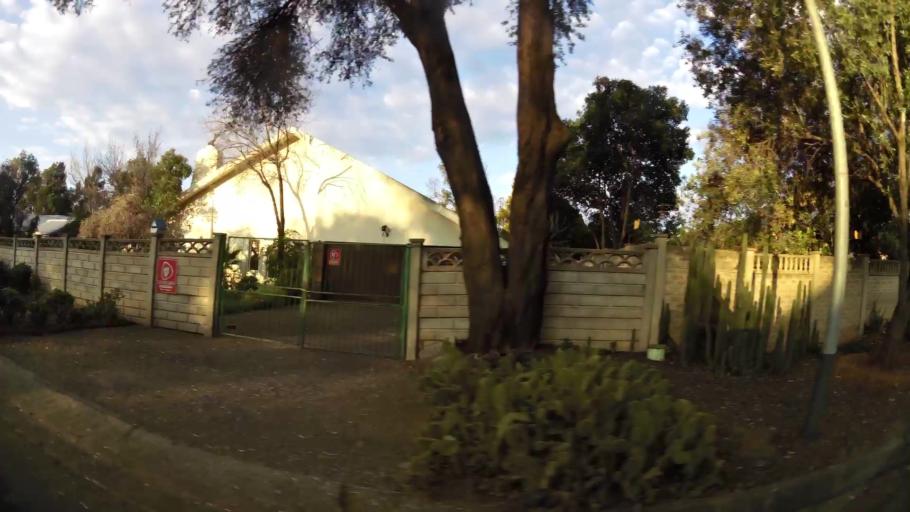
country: ZA
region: Orange Free State
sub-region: Mangaung Metropolitan Municipality
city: Bloemfontein
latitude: -29.1354
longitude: 26.1829
